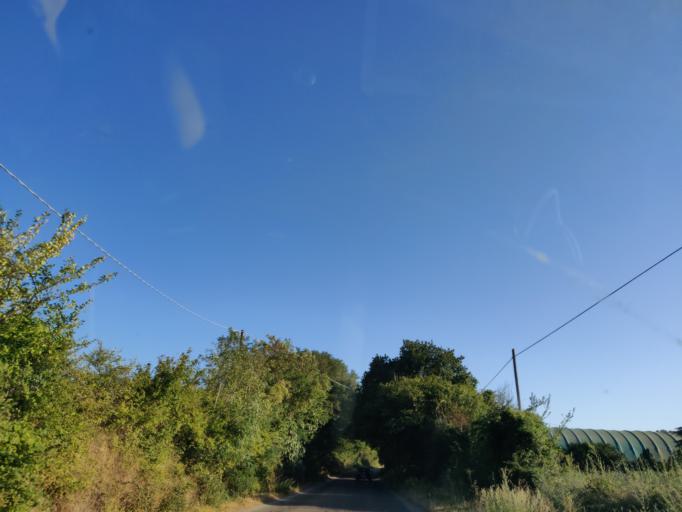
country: IT
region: Latium
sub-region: Provincia di Viterbo
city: Grotte di Castro
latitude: 42.6852
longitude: 11.8753
